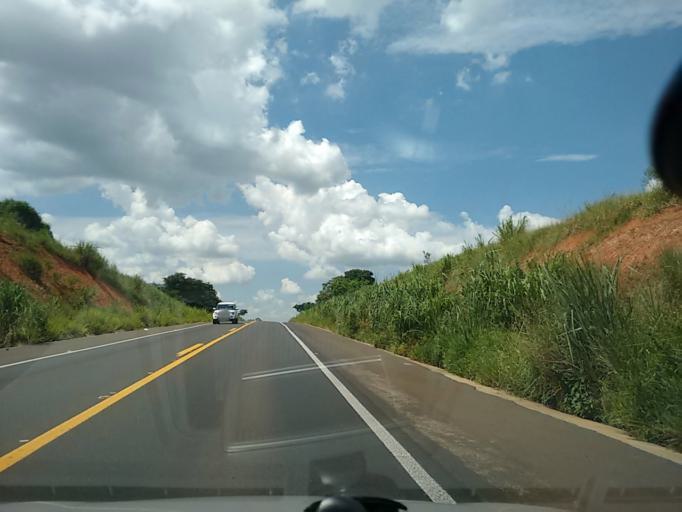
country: BR
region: Sao Paulo
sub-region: Osvaldo Cruz
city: Osvaldo Cruz
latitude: -21.8879
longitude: -50.8706
